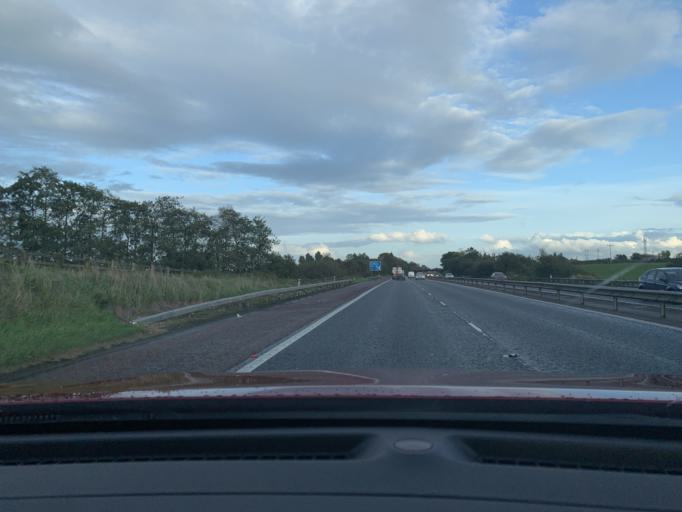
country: GB
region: Northern Ireland
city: Moy
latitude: 54.4806
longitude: -6.5651
